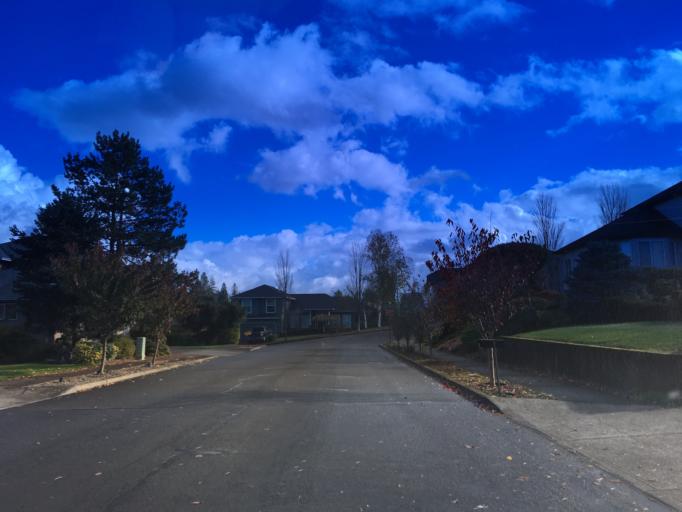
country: US
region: Oregon
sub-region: Multnomah County
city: Troutdale
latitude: 45.5085
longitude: -122.3789
